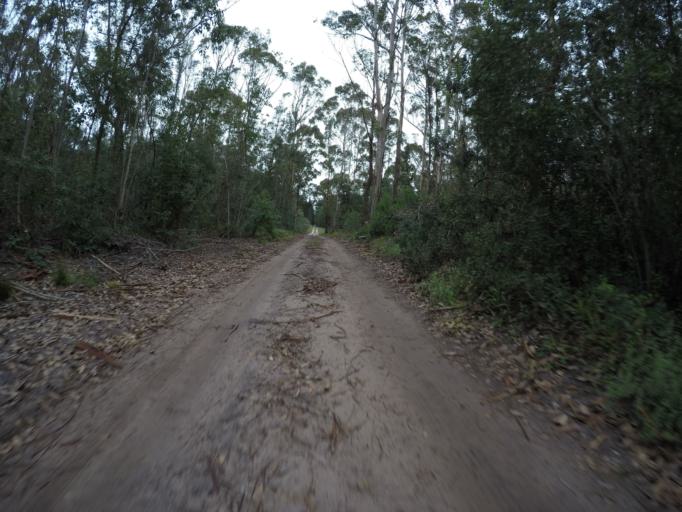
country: ZA
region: Western Cape
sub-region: Eden District Municipality
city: Knysna
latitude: -34.0085
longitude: 22.8102
